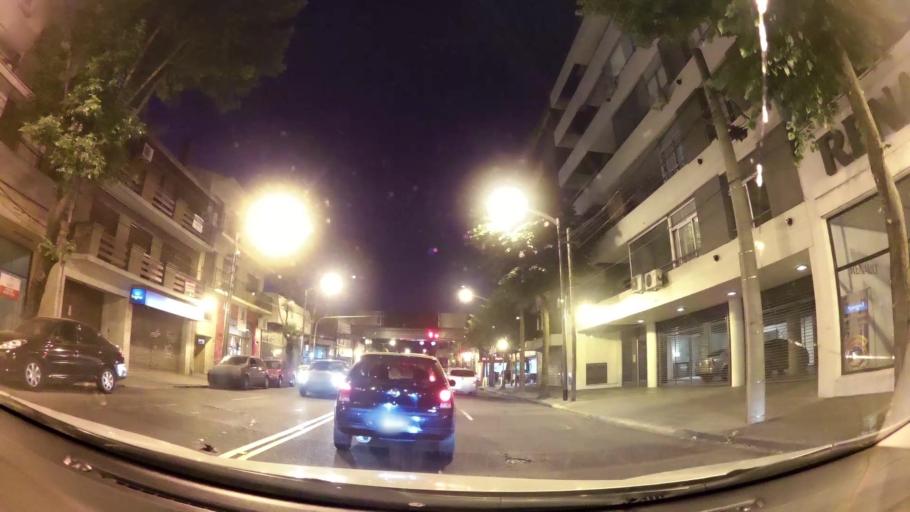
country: AR
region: Buenos Aires
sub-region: Partido de Tigre
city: Tigre
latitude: -34.4475
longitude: -58.5466
